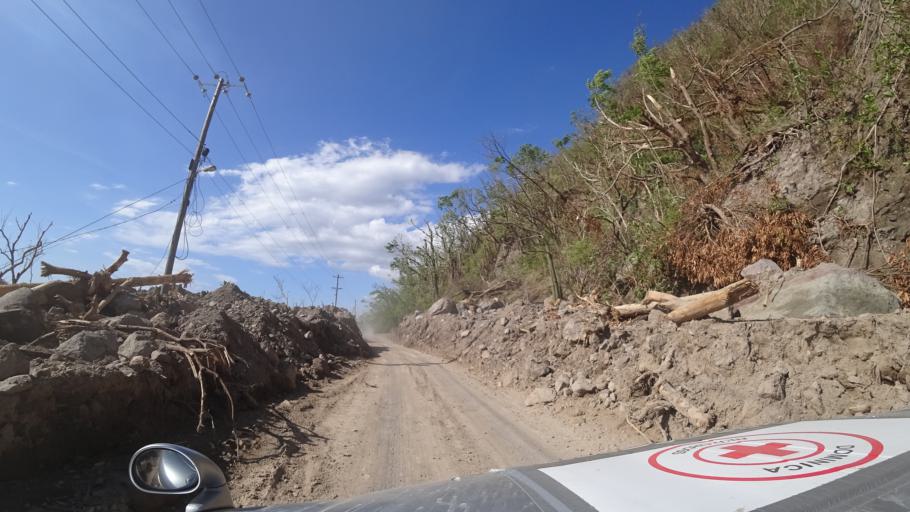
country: DM
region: Saint Luke
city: Pointe Michel
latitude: 15.2510
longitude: -61.3749
